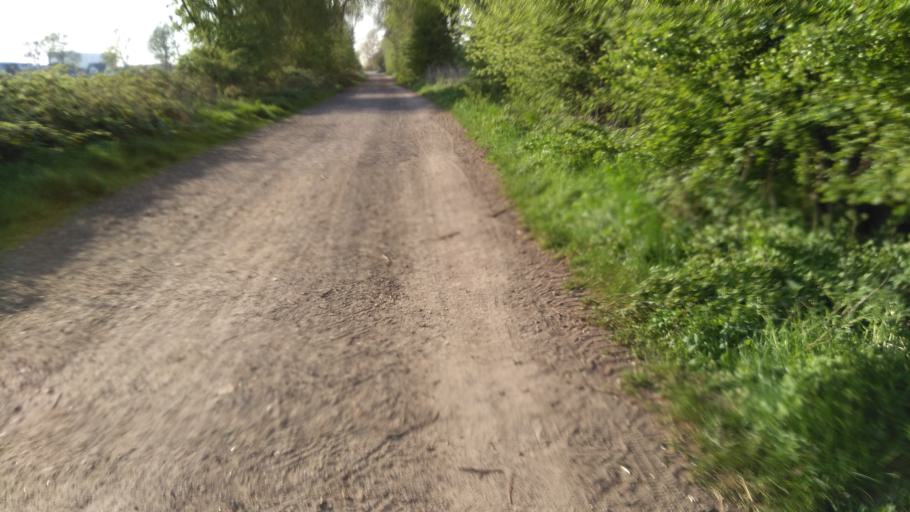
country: DE
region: Lower Saxony
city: Apensen
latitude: 53.4417
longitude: 9.6343
